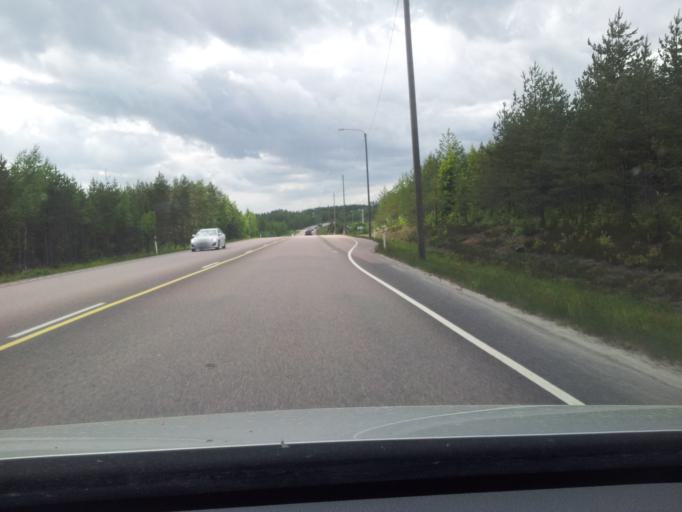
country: FI
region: South Karelia
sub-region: Lappeenranta
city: Taavetti
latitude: 60.9167
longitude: 27.4497
